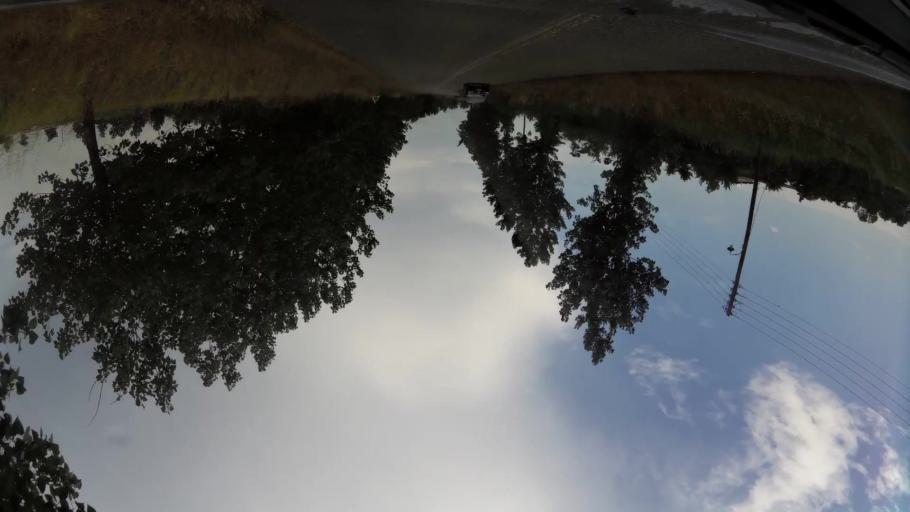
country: GR
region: Central Macedonia
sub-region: Nomos Pierias
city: Paralia
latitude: 40.2802
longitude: 22.6007
